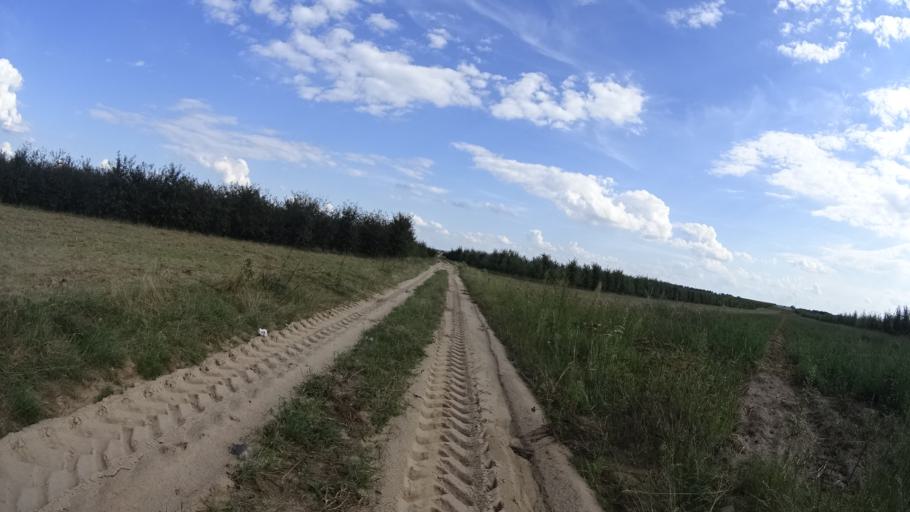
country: PL
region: Masovian Voivodeship
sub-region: Powiat bialobrzeski
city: Wysmierzyce
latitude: 51.6666
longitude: 20.8112
